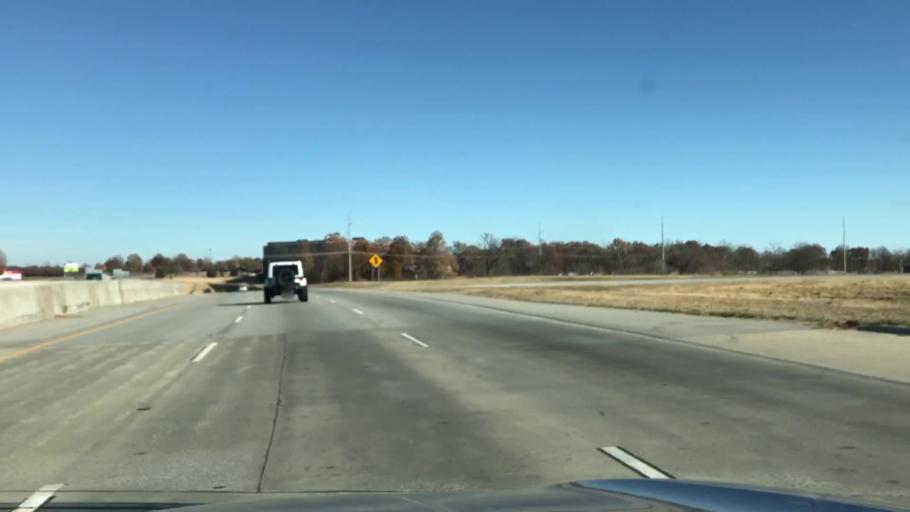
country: US
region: Arkansas
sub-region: Benton County
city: Lowell
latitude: 36.2408
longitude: -94.1547
